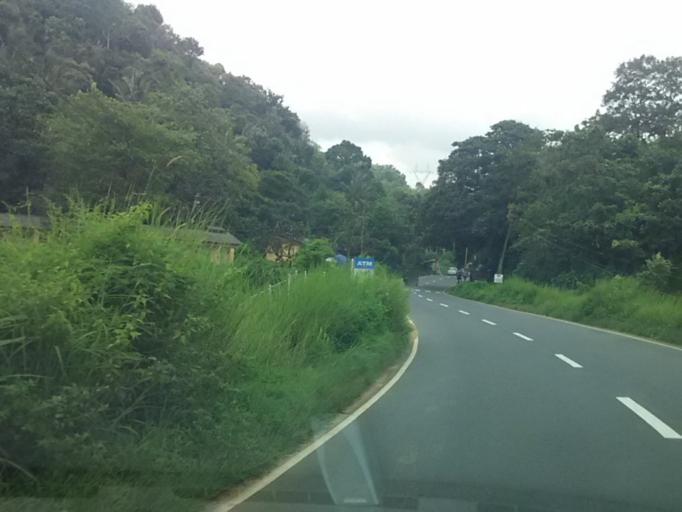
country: IN
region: Kerala
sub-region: Wayanad
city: Kalpetta
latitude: 11.5481
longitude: 76.0393
